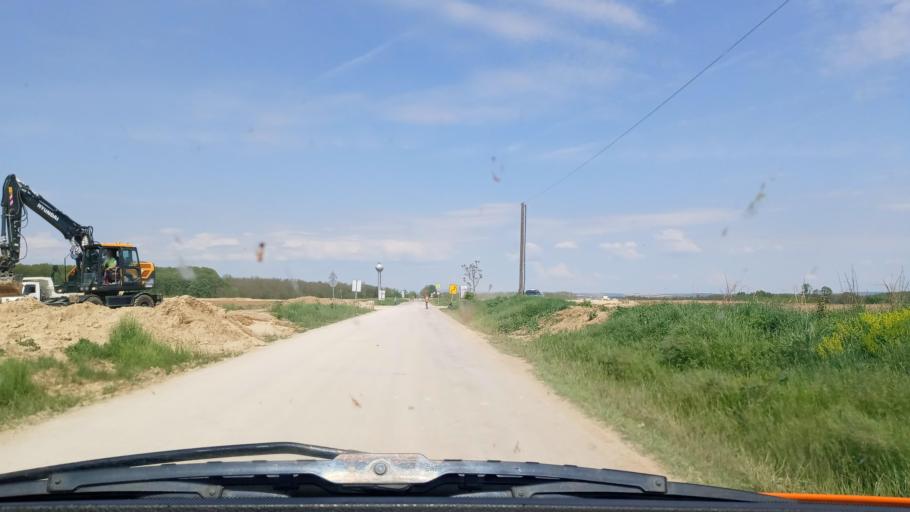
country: HU
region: Baranya
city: Boly
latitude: 45.8895
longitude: 18.5628
